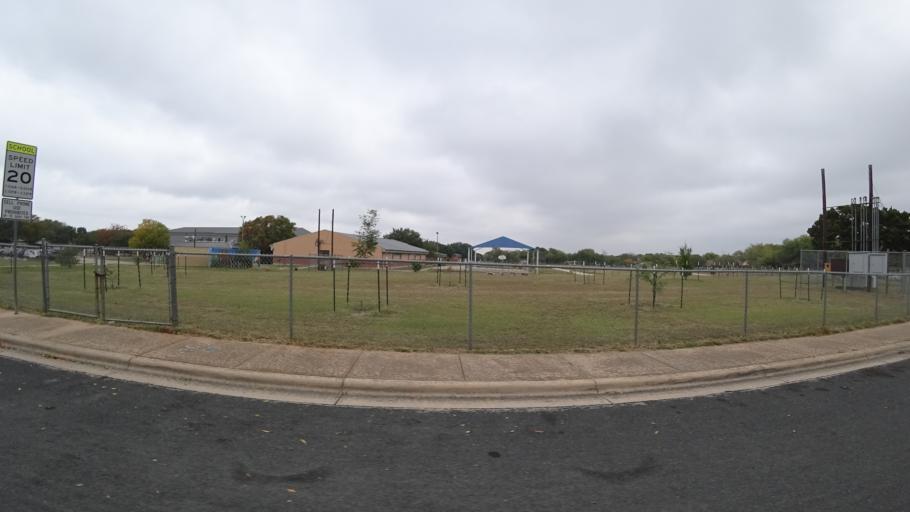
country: US
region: Texas
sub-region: Travis County
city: Shady Hollow
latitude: 30.2025
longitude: -97.8401
